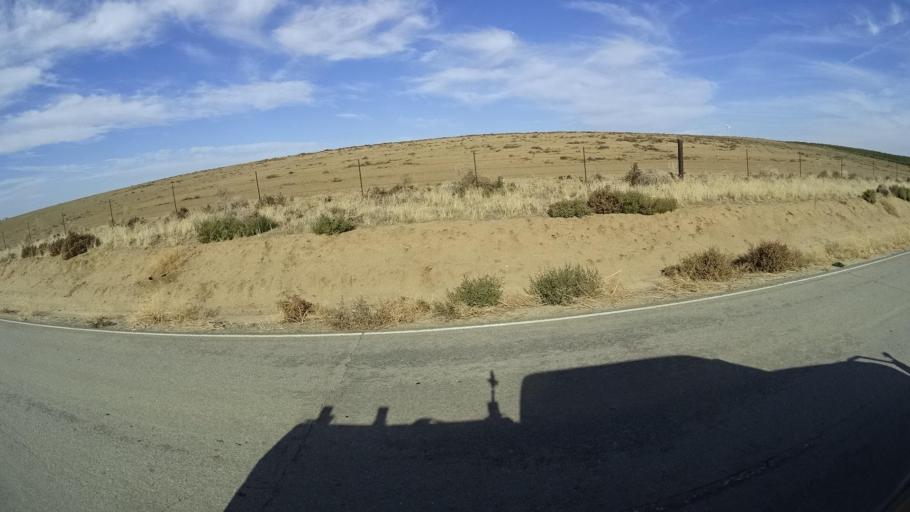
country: US
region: California
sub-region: Kern County
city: McFarland
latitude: 35.6155
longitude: -119.0511
